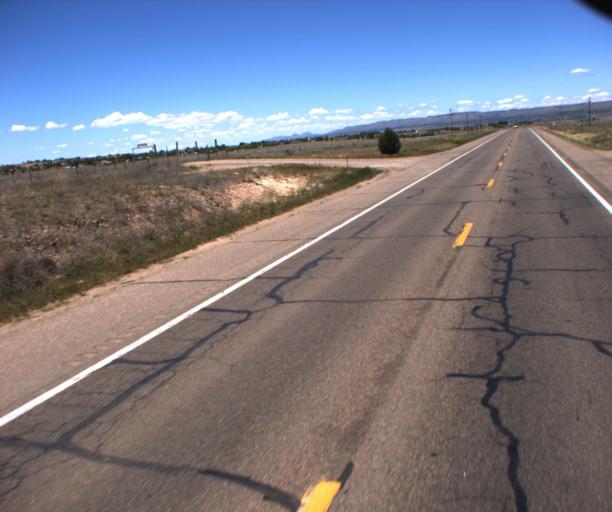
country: US
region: Arizona
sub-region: Yavapai County
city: Paulden
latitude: 34.8489
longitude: -112.4663
